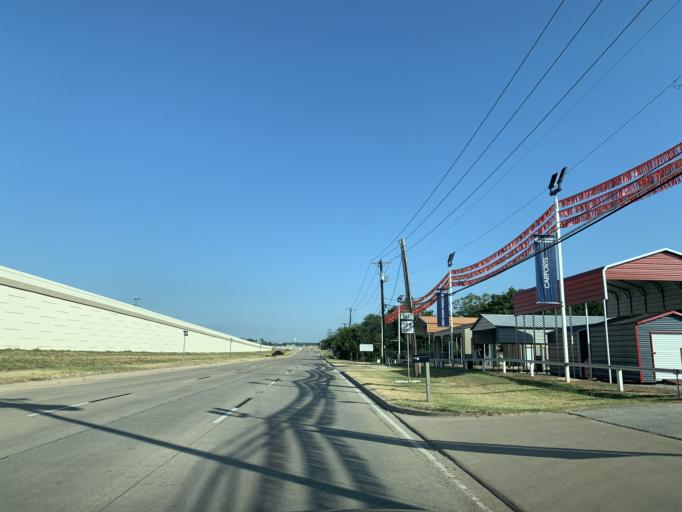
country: US
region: Texas
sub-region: Tarrant County
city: Lakeside
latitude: 32.8385
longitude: -97.4916
